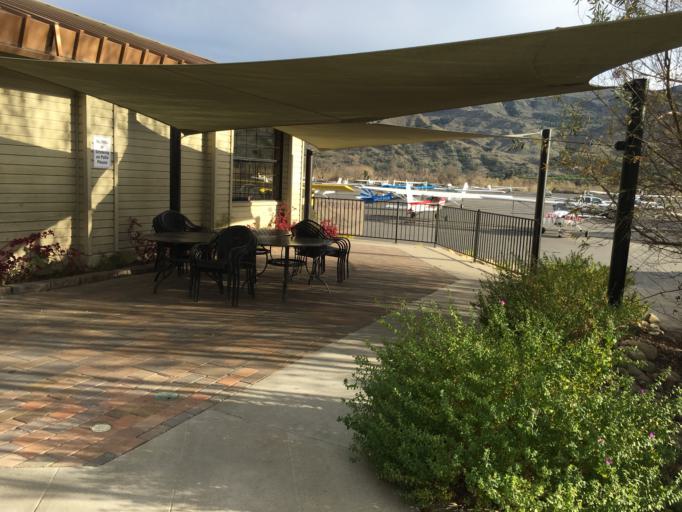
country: US
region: California
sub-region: Ventura County
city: Santa Paula
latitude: 34.3486
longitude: -119.0615
